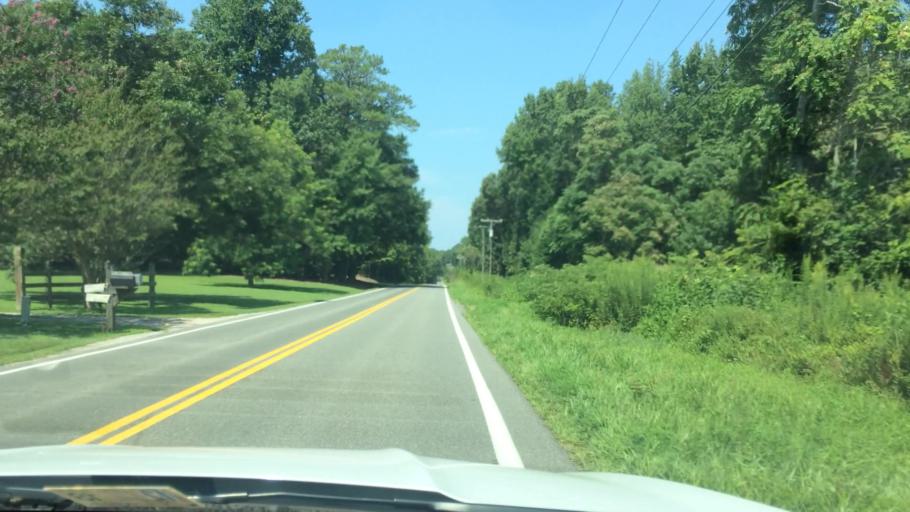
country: US
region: Virginia
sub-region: New Kent County
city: New Kent
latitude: 37.5255
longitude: -77.0143
